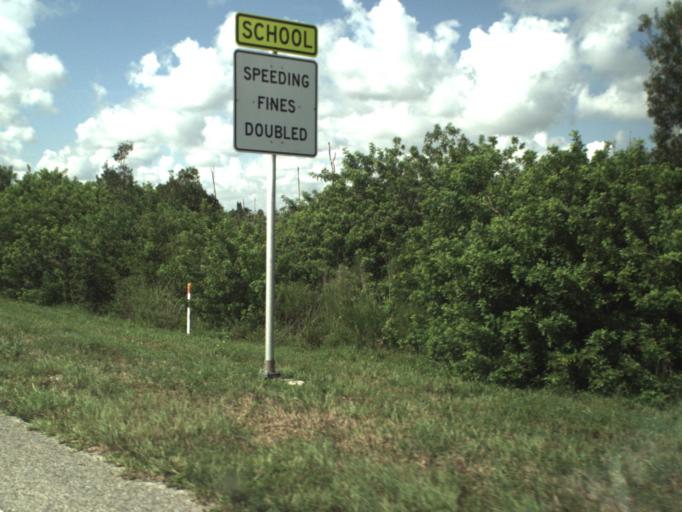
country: US
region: Florida
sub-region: Broward County
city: Weston
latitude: 26.0190
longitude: -80.4332
